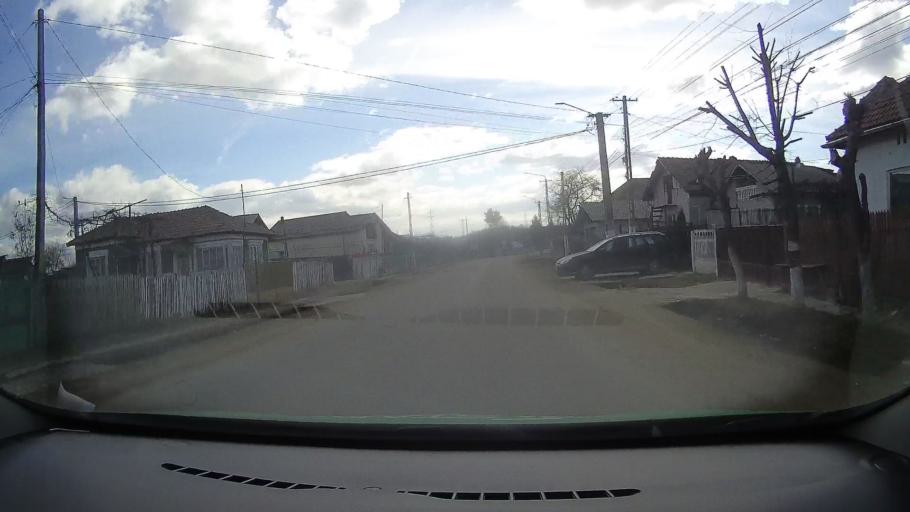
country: RO
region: Dambovita
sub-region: Comuna Doicesti
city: Doicesti
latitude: 44.9774
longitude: 25.3917
